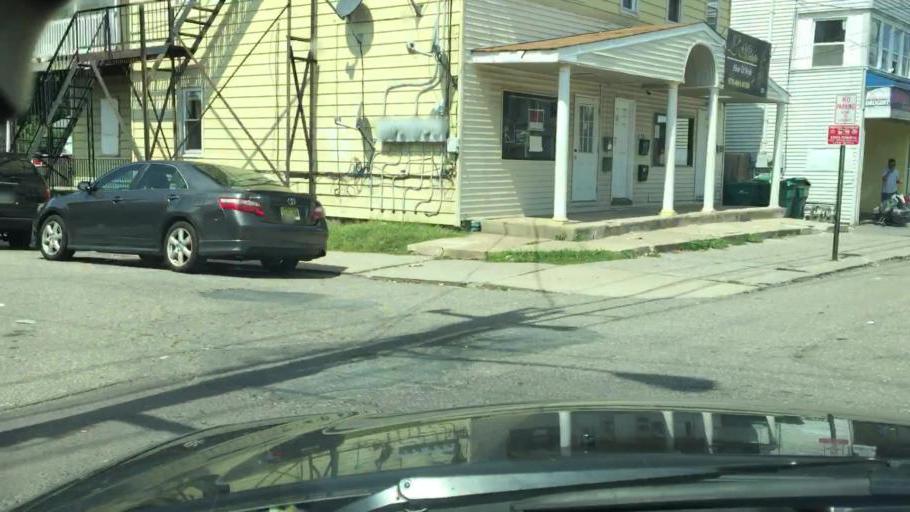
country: US
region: Pennsylvania
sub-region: Luzerne County
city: Hazleton
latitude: 40.9611
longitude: -75.9781
